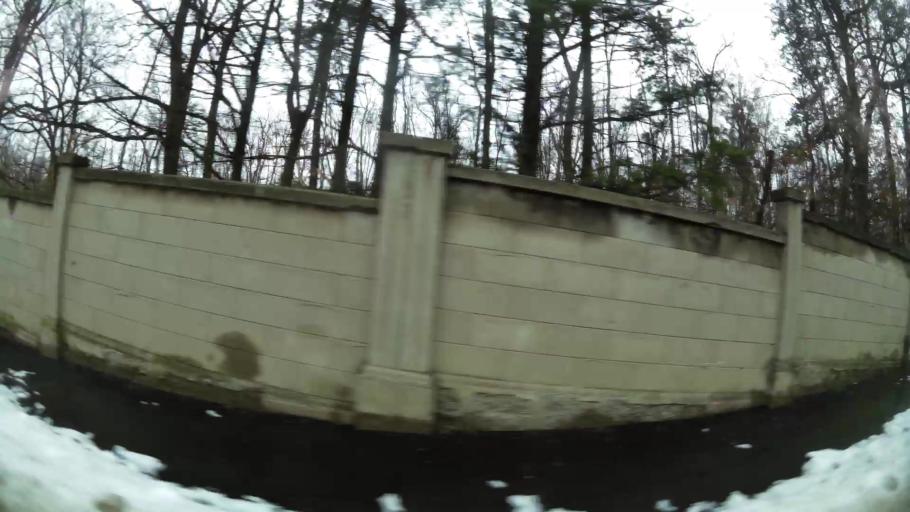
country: RS
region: Central Serbia
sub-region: Belgrade
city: Savski Venac
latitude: 44.7612
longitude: 20.4532
